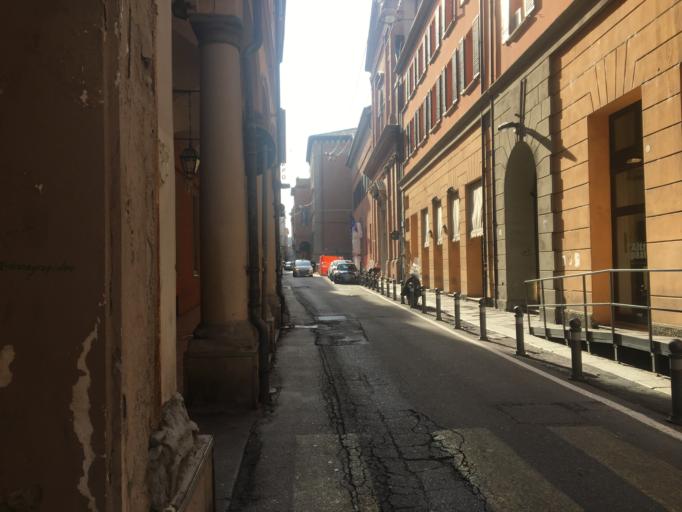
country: IT
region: Emilia-Romagna
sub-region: Provincia di Bologna
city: Bologna
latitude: 44.4978
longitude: 11.3396
